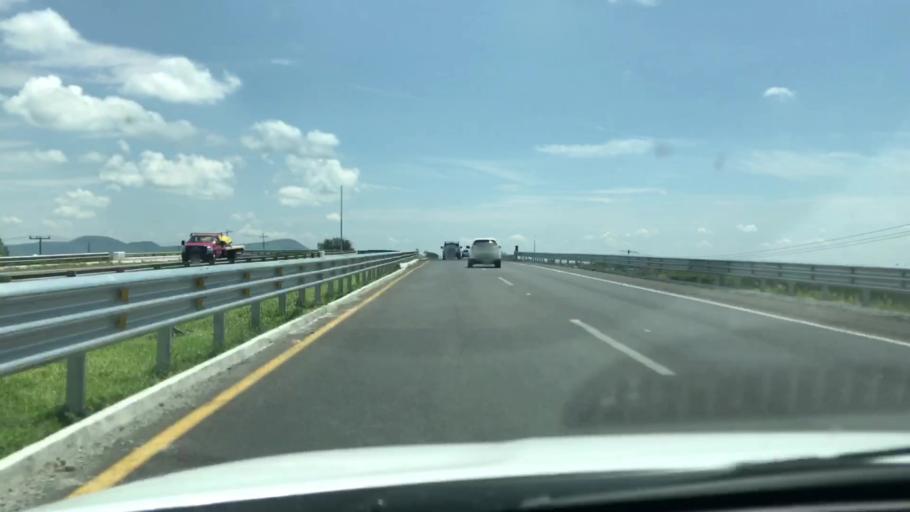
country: MX
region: Guanajuato
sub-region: Irapuato
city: Cuarta Brigada
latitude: 20.6522
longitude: -101.3159
